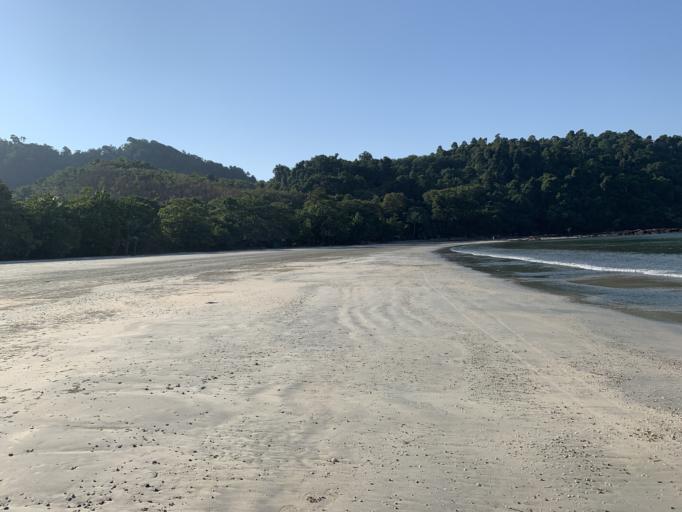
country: TH
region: Ranong
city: Kapoe
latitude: 9.7128
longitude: 98.3969
